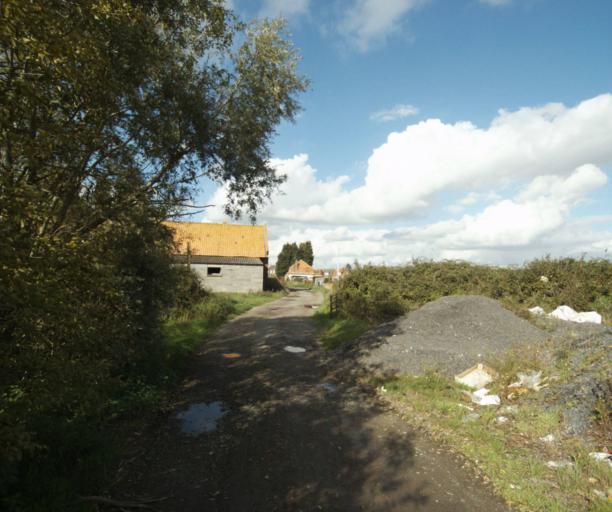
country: FR
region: Nord-Pas-de-Calais
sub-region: Departement du Nord
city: Frelinghien
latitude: 50.7056
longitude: 2.9348
